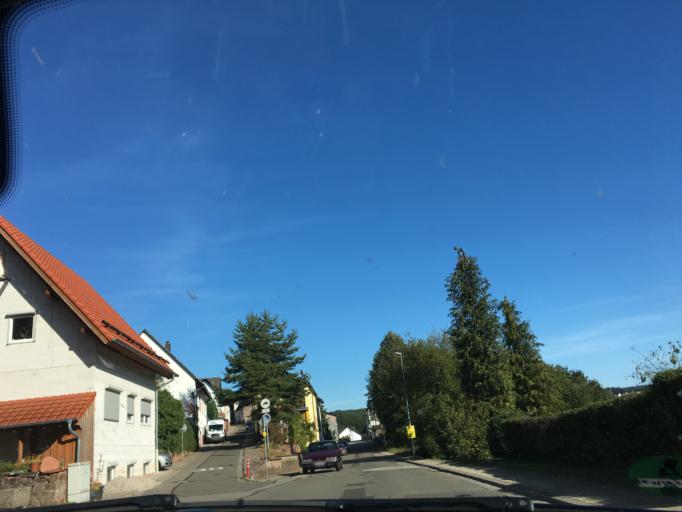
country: DE
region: Rheinland-Pfalz
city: Krickenbach
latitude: 49.3614
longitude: 7.6695
